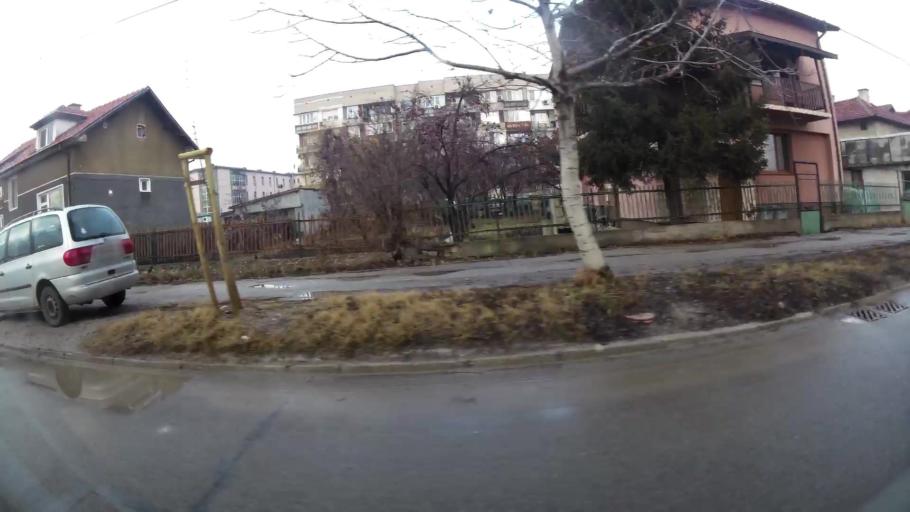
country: BG
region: Sofia-Capital
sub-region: Stolichna Obshtina
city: Sofia
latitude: 42.7423
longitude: 23.3456
